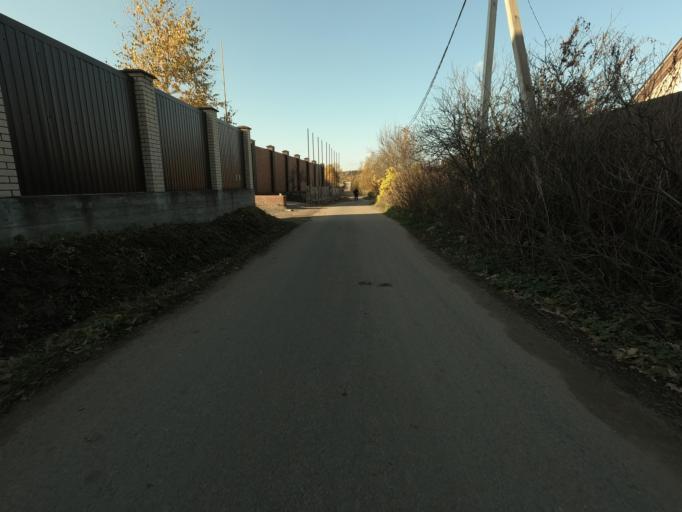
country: RU
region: Leningrad
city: Luppolovo
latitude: 60.1386
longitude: 30.2545
